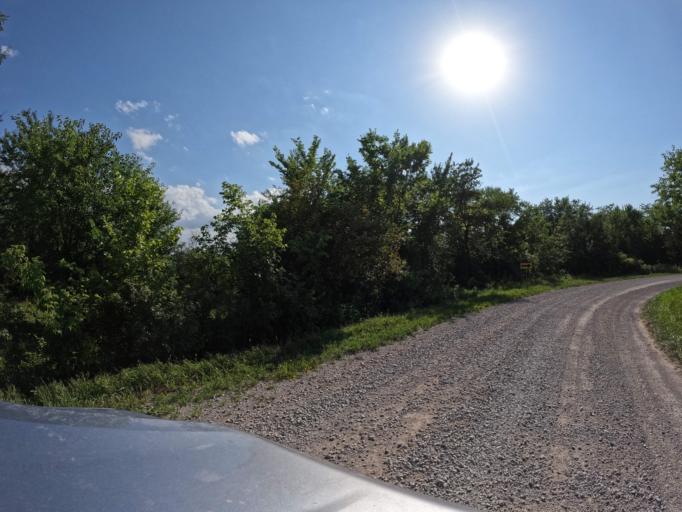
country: US
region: Iowa
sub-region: Appanoose County
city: Centerville
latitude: 40.7322
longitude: -93.0201
